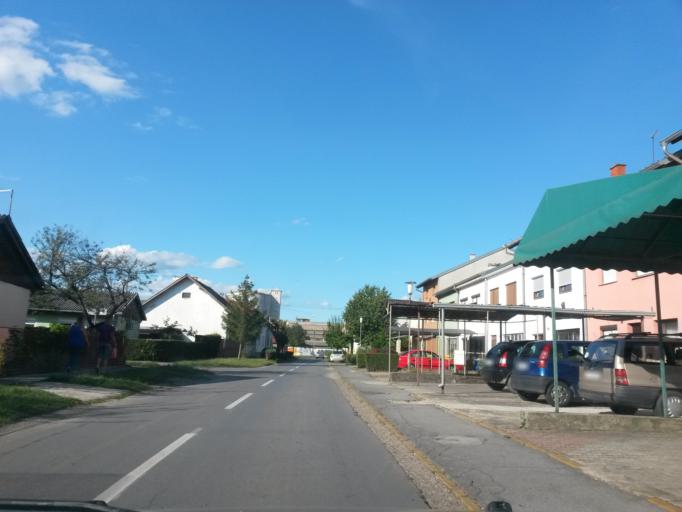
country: HR
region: Osjecko-Baranjska
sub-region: Grad Osijek
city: Osijek
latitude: 45.5476
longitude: 18.7223
